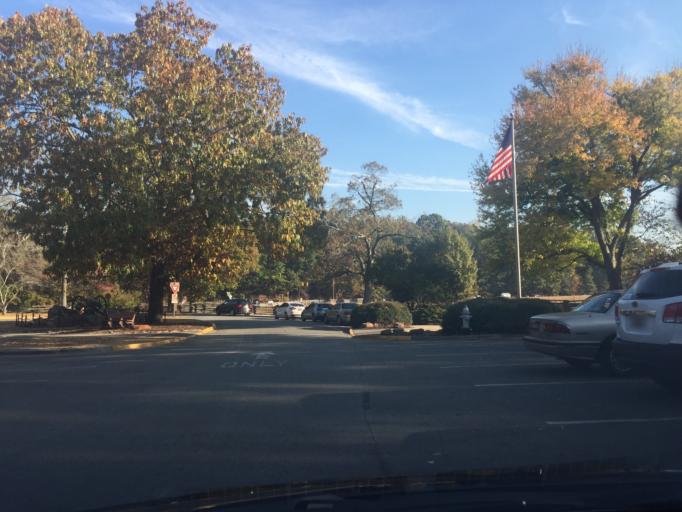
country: US
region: Georgia
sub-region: Cobb County
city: Marietta
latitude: 33.9831
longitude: -84.5786
